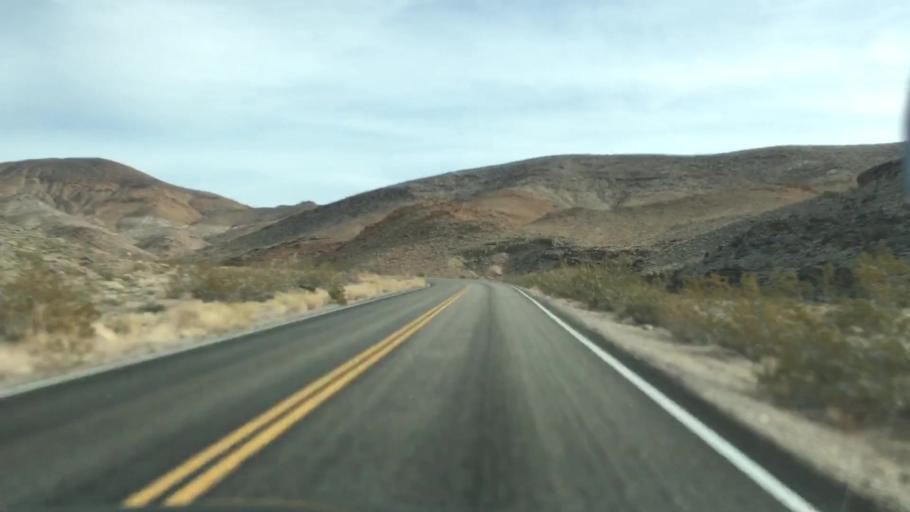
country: US
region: Nevada
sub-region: Nye County
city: Beatty
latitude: 36.7438
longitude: -116.9575
